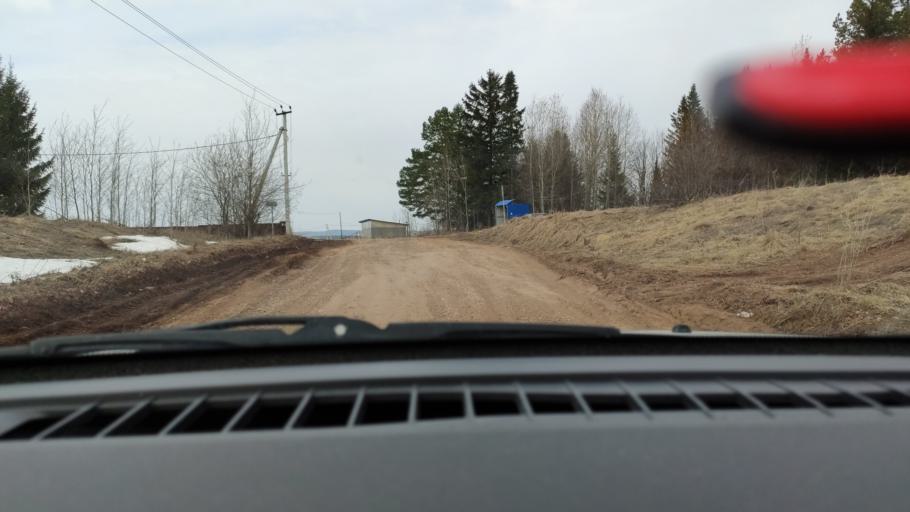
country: RU
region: Perm
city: Kultayevo
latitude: 57.8981
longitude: 56.0118
